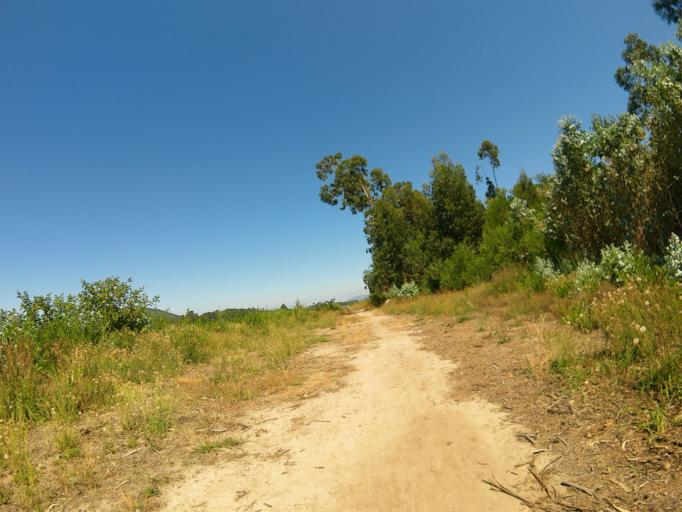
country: PT
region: Viana do Castelo
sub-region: Viana do Castelo
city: Darque
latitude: 41.6938
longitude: -8.7705
